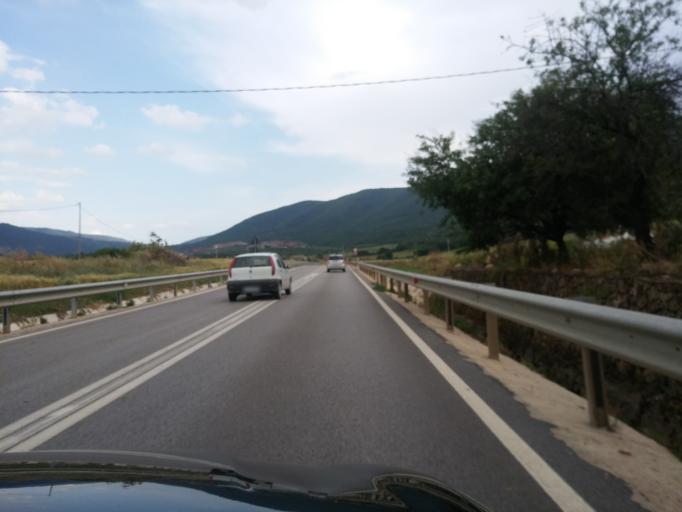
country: IT
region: Apulia
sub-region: Provincia di Foggia
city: Rignano Garganico
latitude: 41.7146
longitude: 15.5305
